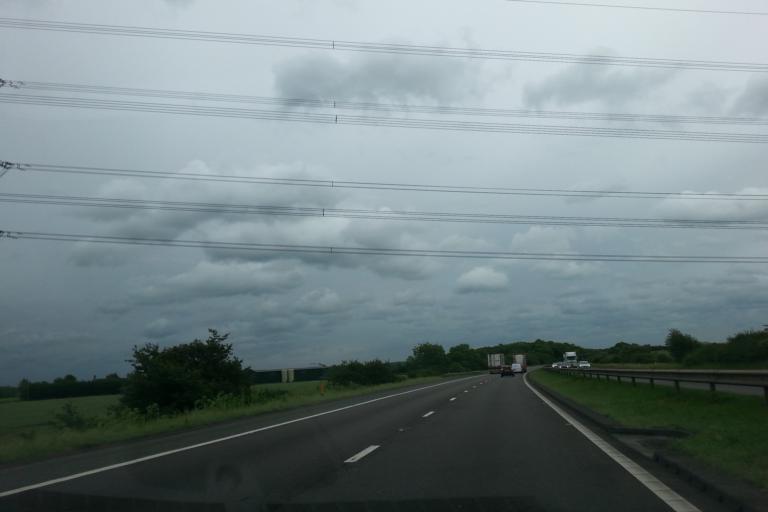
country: GB
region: England
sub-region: Doncaster
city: Tickhill
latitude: 53.4546
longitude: -1.1167
